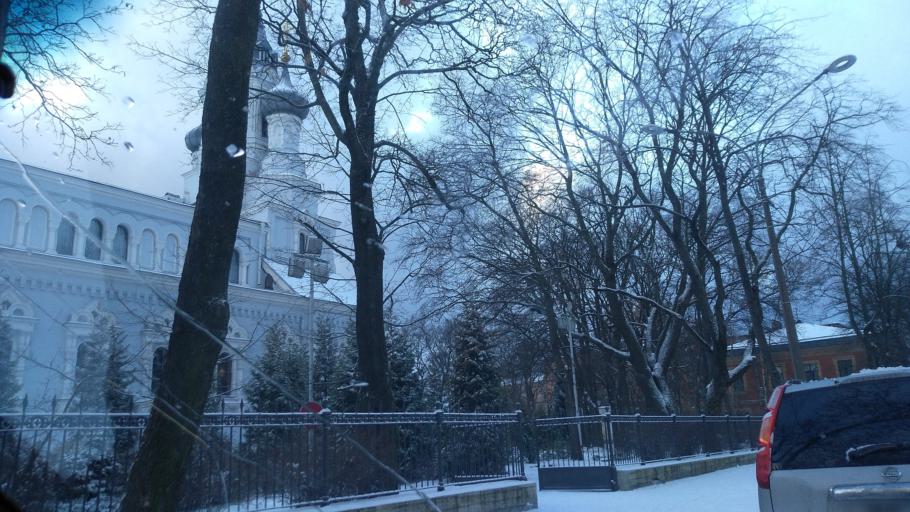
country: RU
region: St.-Petersburg
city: Kronshtadt
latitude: 59.9988
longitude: 29.7672
